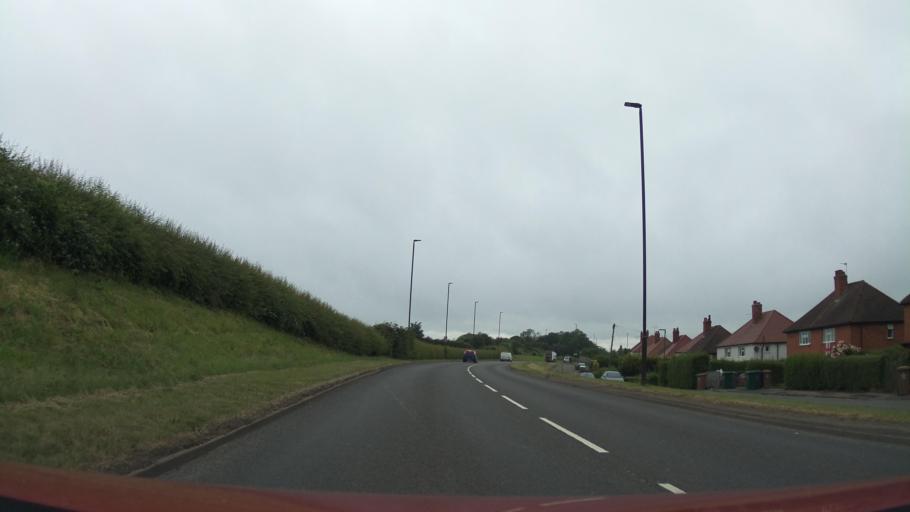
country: GB
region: England
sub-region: Derbyshire
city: Swadlincote
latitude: 52.7620
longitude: -1.5897
